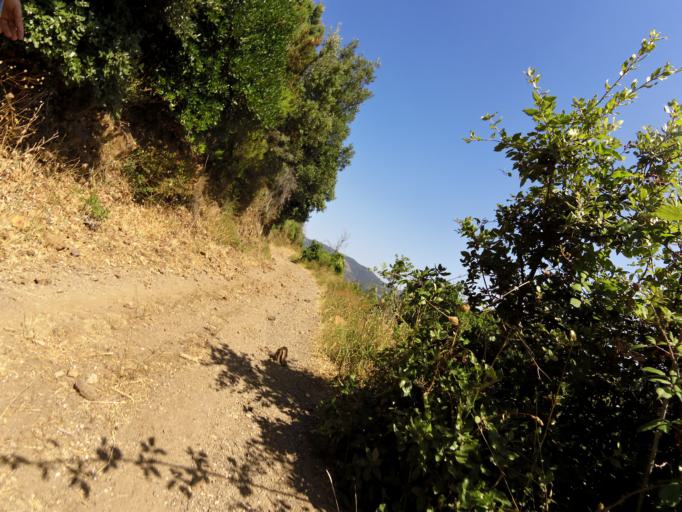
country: IT
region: Calabria
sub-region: Provincia di Reggio Calabria
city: Bivongi
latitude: 38.5018
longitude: 16.4477
